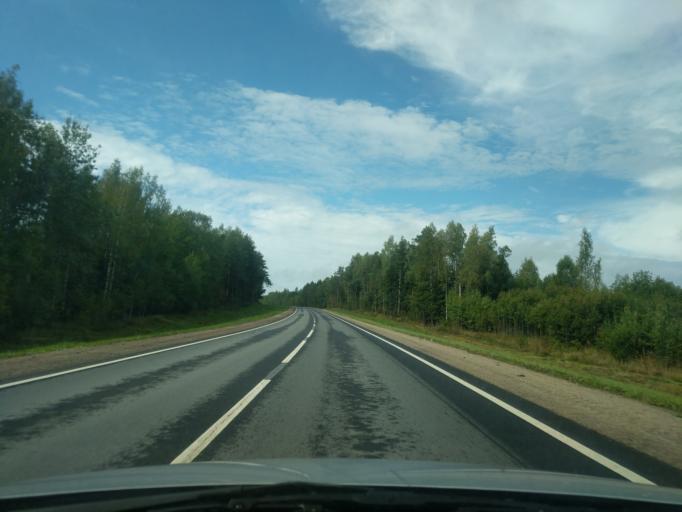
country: RU
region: Kostroma
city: Sudislavl'
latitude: 57.8327
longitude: 41.8801
